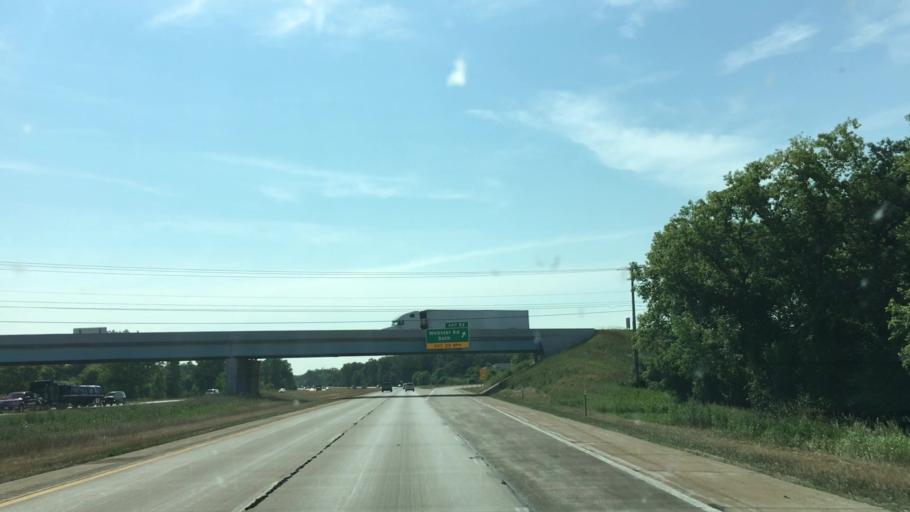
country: US
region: Michigan
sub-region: Clinton County
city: Bath
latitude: 42.7977
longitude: -84.4499
